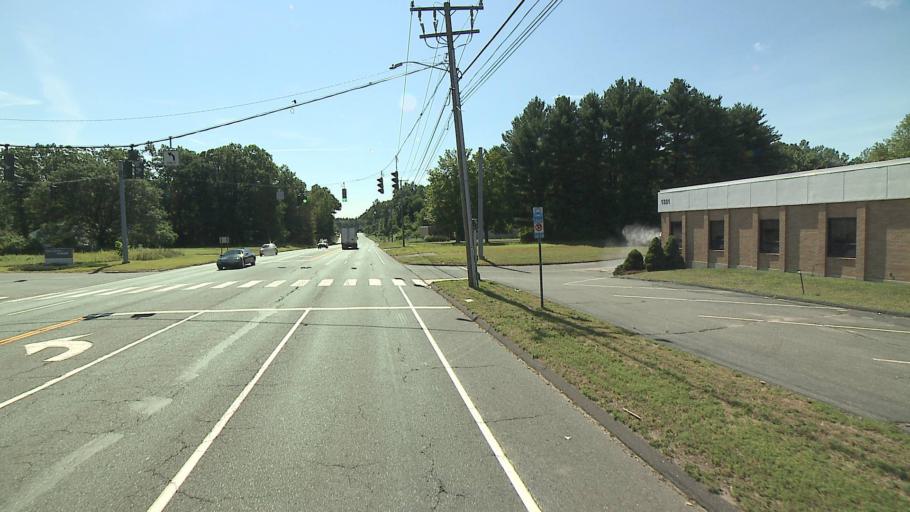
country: US
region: Connecticut
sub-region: Hartford County
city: Blue Hills
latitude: 41.8583
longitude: -72.7095
